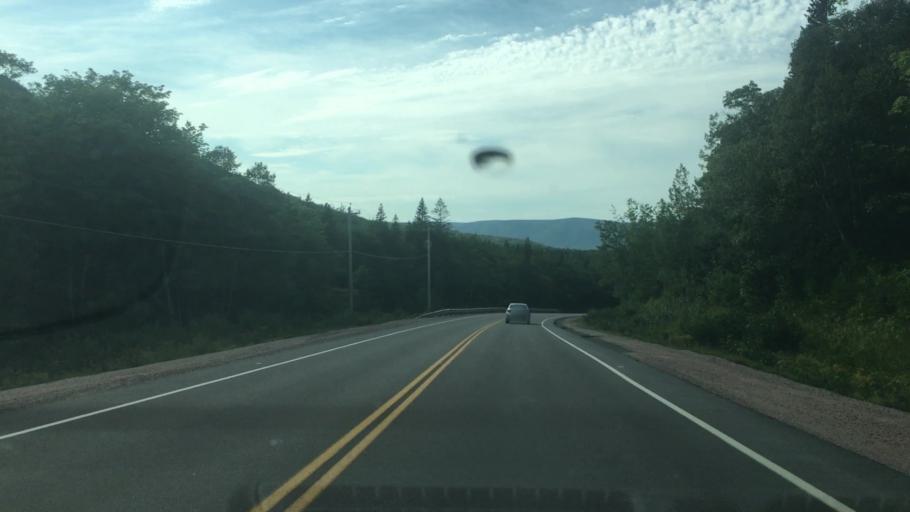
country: CA
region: Nova Scotia
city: Sydney Mines
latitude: 46.8555
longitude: -60.4562
